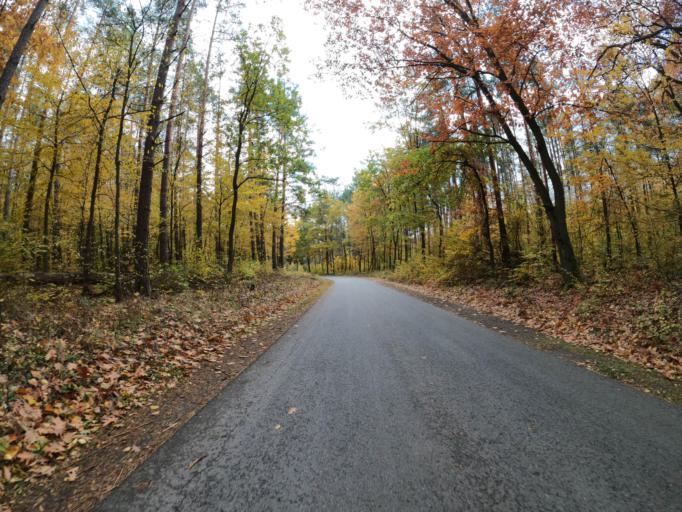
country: PL
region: West Pomeranian Voivodeship
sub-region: Powiat mysliborski
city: Barlinek
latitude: 52.9338
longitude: 15.2853
